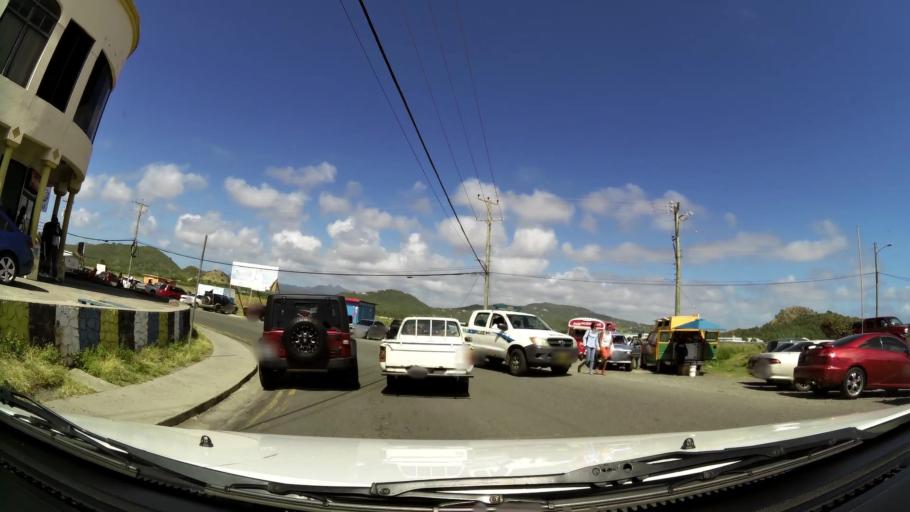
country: LC
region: Vieux-Fort
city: Vieux Fort
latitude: 13.7314
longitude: -60.9516
